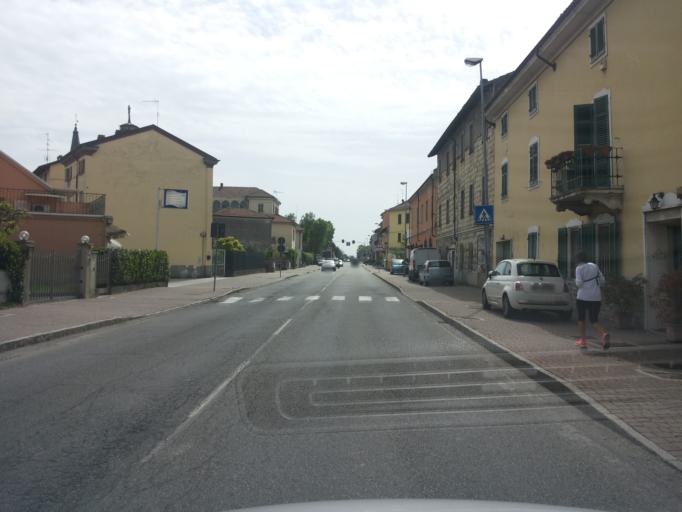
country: IT
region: Piedmont
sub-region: Provincia di Alessandria
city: Terruggia
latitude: 45.0994
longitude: 8.4541
